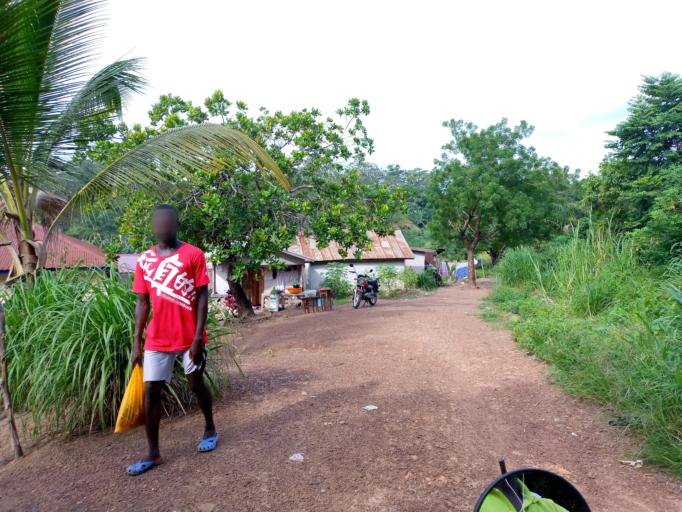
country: SL
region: Northern Province
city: Magburaka
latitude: 8.7177
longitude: -11.9475
